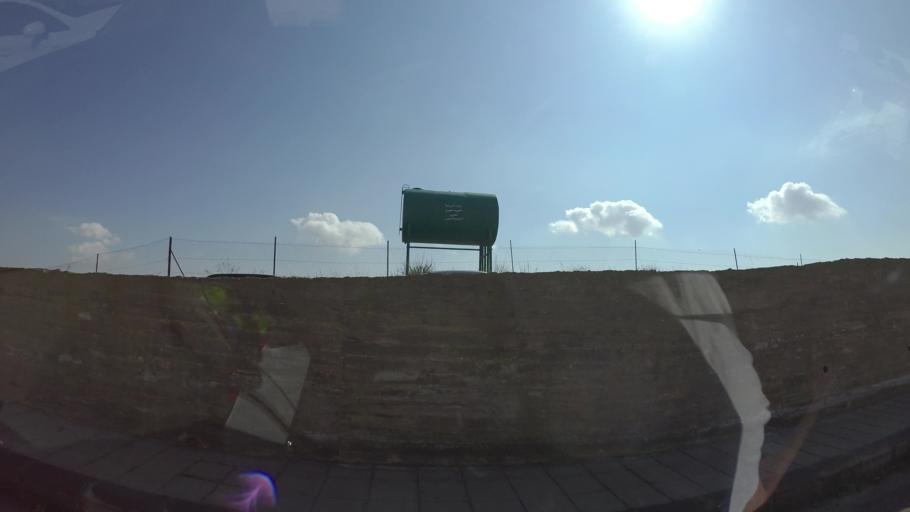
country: JO
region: Amman
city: Al Jubayhah
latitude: 31.9987
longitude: 35.9031
